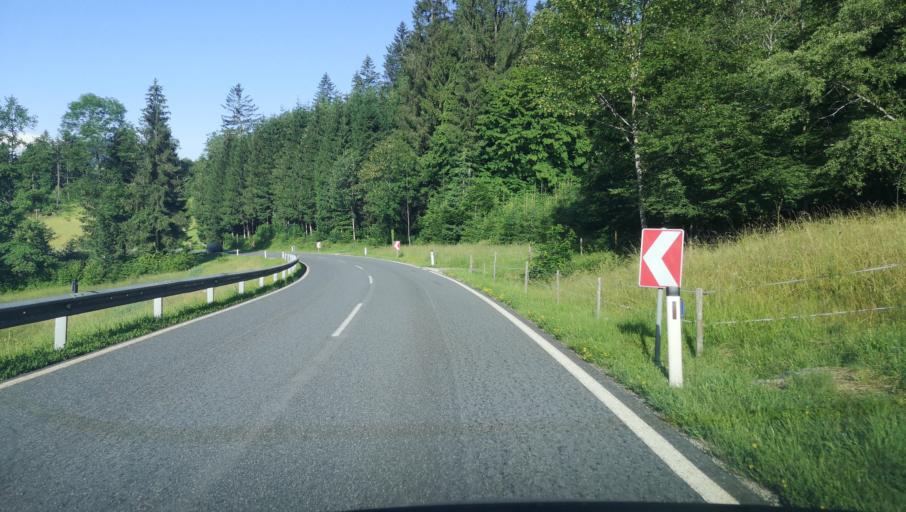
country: AT
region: Lower Austria
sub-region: Politischer Bezirk Scheibbs
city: Randegg
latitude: 47.9654
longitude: 14.9414
